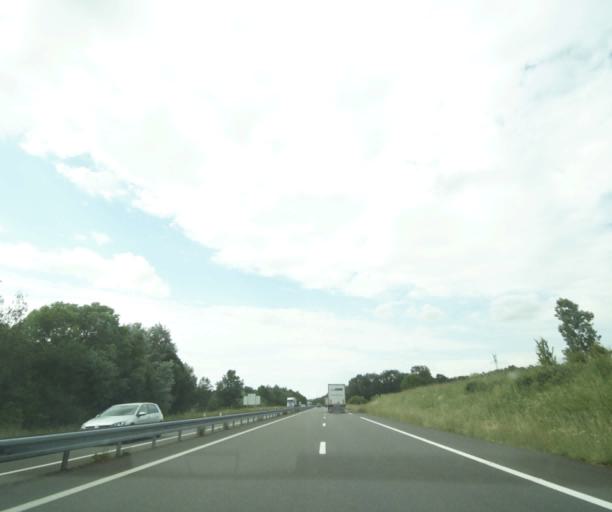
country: FR
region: Pays de la Loire
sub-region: Departement de Maine-et-Loire
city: Brion
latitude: 47.4625
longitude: -0.1839
